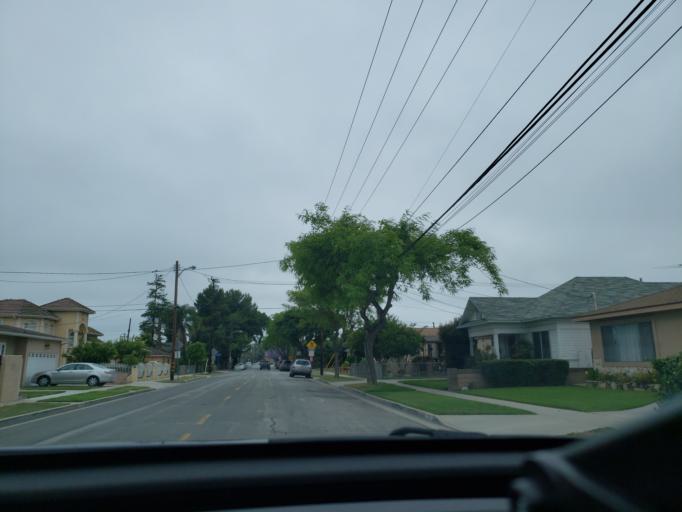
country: US
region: California
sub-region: Los Angeles County
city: Artesia
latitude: 33.8628
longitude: -118.0836
